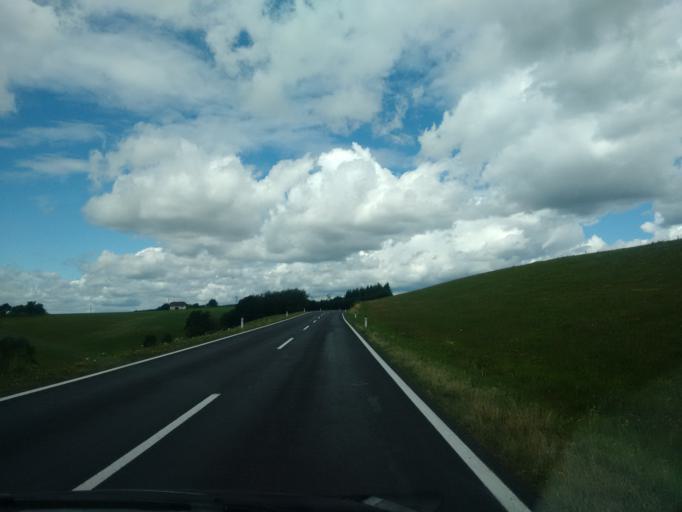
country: AT
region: Upper Austria
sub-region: Politischer Bezirk Urfahr-Umgebung
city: Gramastetten
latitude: 48.4094
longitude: 14.1698
